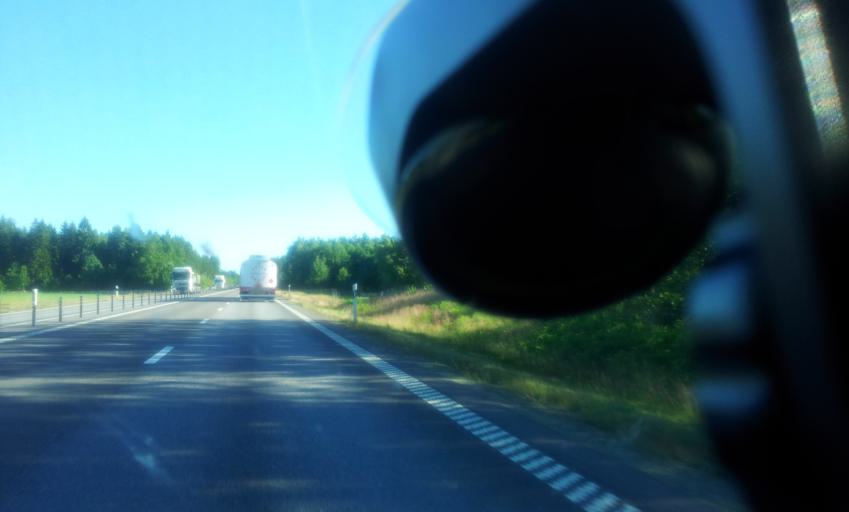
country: SE
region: Kalmar
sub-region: Torsas Kommun
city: Torsas
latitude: 56.5163
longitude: 16.0858
